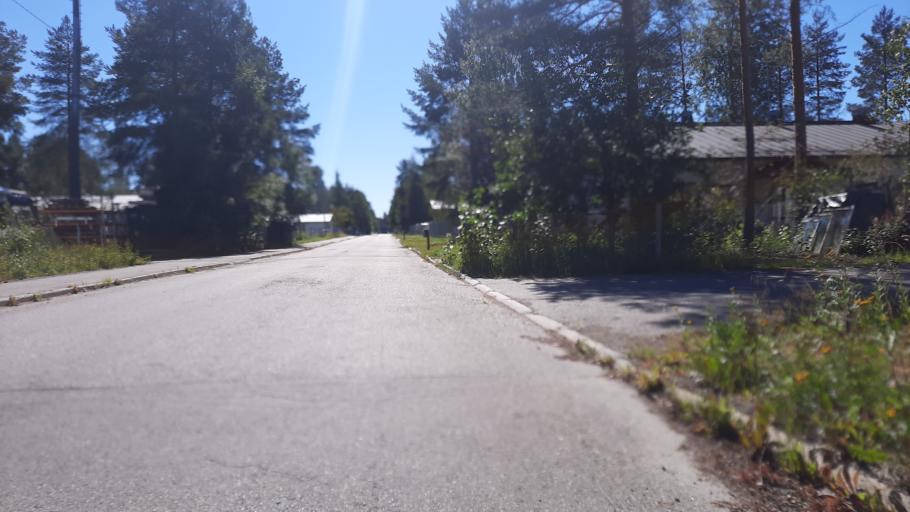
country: FI
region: North Karelia
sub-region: Joensuu
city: Joensuu
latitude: 62.6242
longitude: 29.7437
